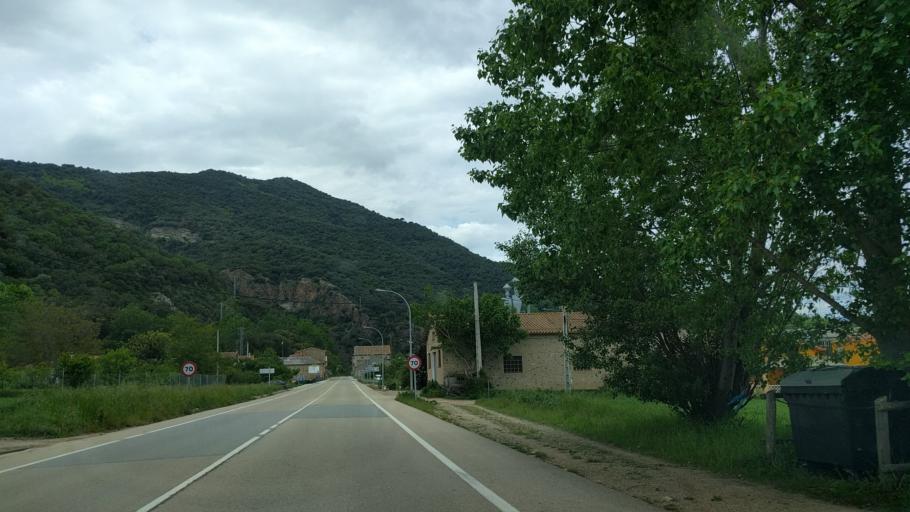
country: ES
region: Catalonia
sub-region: Provincia de Girona
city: la Cellera de Ter
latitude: 41.9822
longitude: 2.6084
